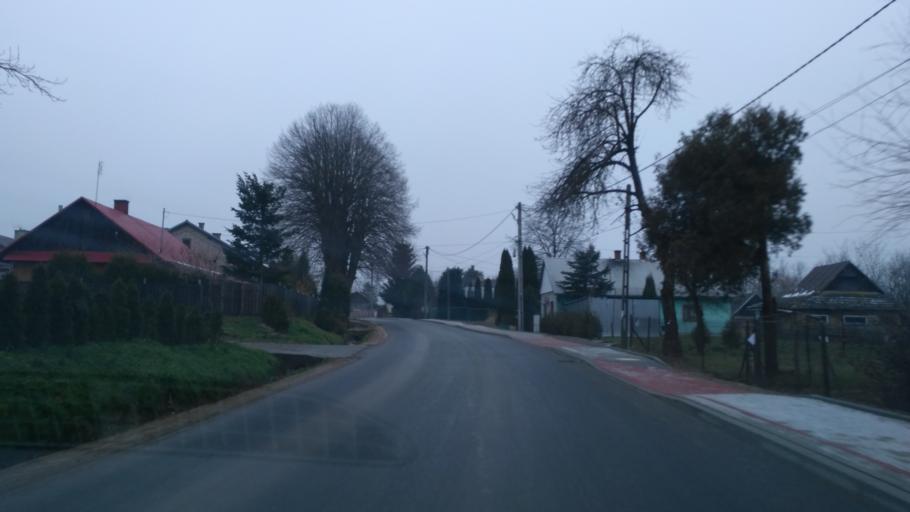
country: PL
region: Subcarpathian Voivodeship
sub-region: Powiat przeworski
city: Kanczuga
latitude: 50.0159
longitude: 22.4135
